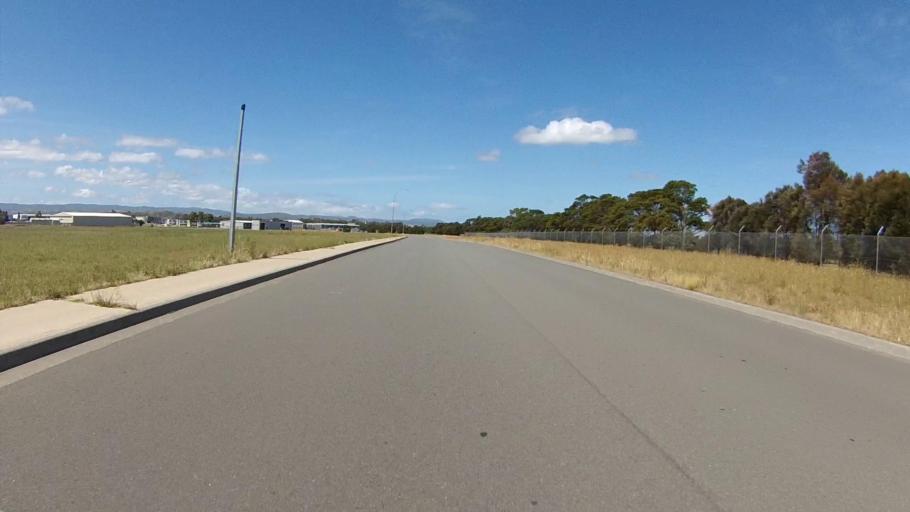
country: AU
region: Tasmania
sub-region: Clarence
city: Cambridge
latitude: -42.8345
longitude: 147.4769
